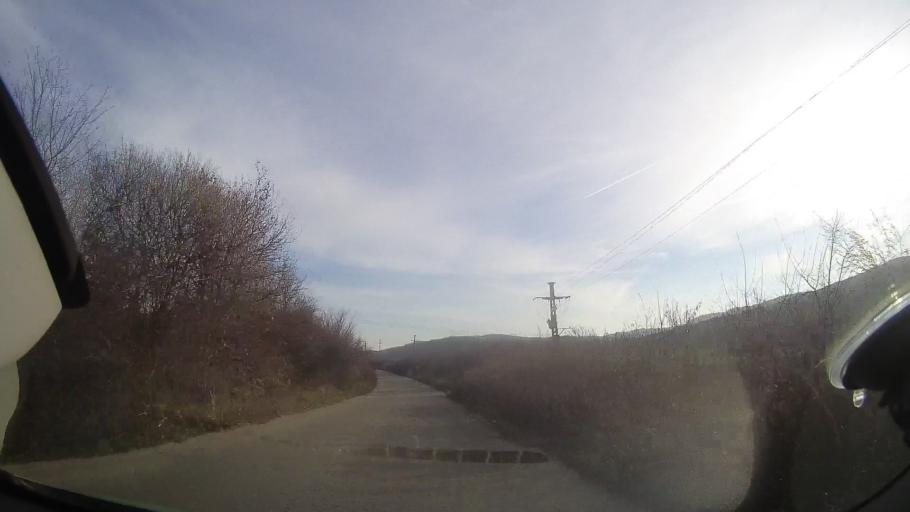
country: RO
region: Bihor
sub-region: Comuna Sarbi
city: Sarbi
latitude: 47.1836
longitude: 22.1310
